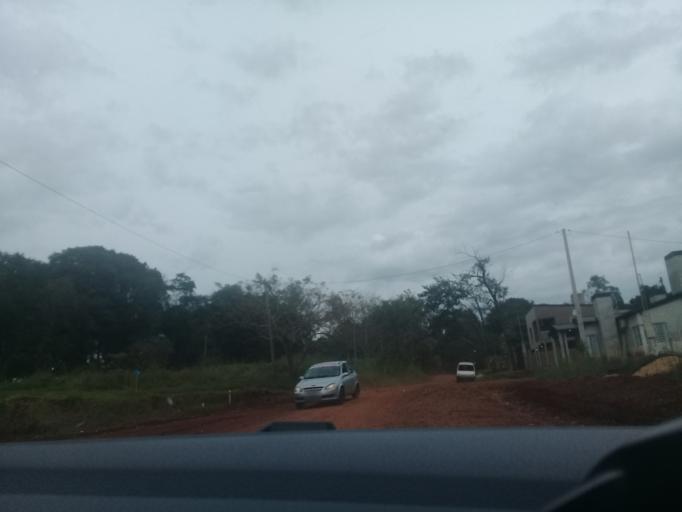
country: AR
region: Misiones
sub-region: Departamento de Obera
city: Obera
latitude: -27.4782
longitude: -55.1520
